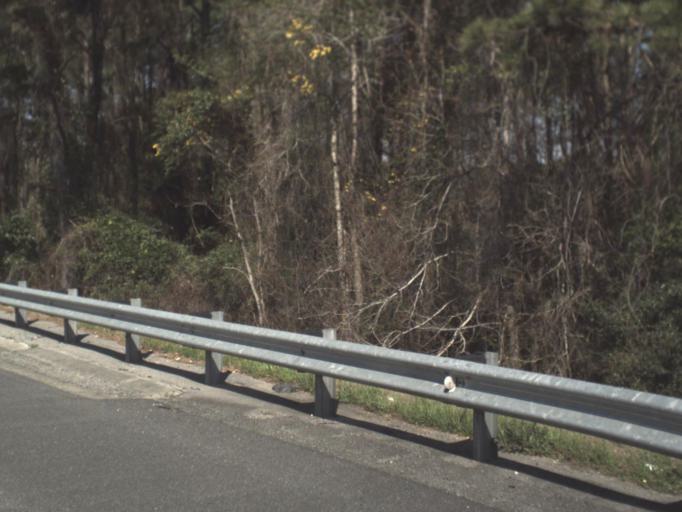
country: US
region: Florida
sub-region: Jackson County
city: Marianna
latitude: 30.7284
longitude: -85.2180
